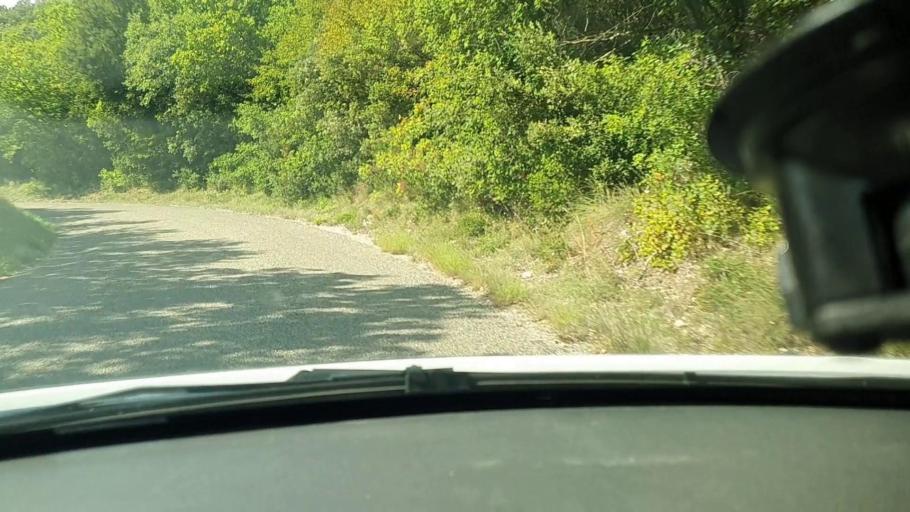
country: FR
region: Languedoc-Roussillon
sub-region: Departement du Gard
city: Goudargues
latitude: 44.1576
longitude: 4.4216
